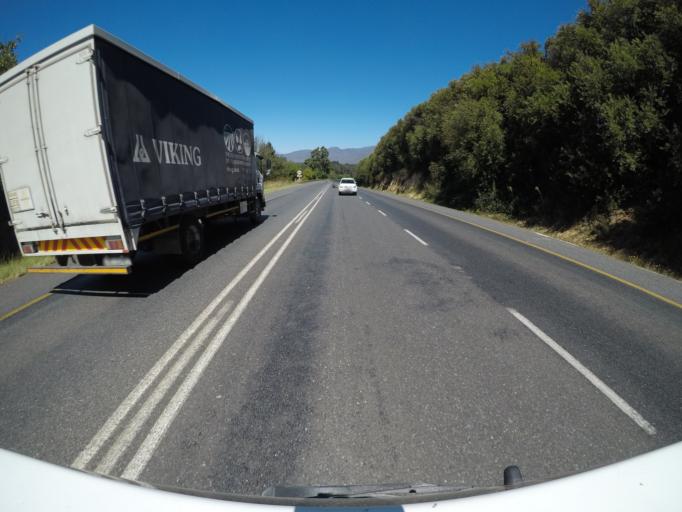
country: ZA
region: Western Cape
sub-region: Overberg District Municipality
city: Grabouw
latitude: -34.1635
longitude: 19.0278
